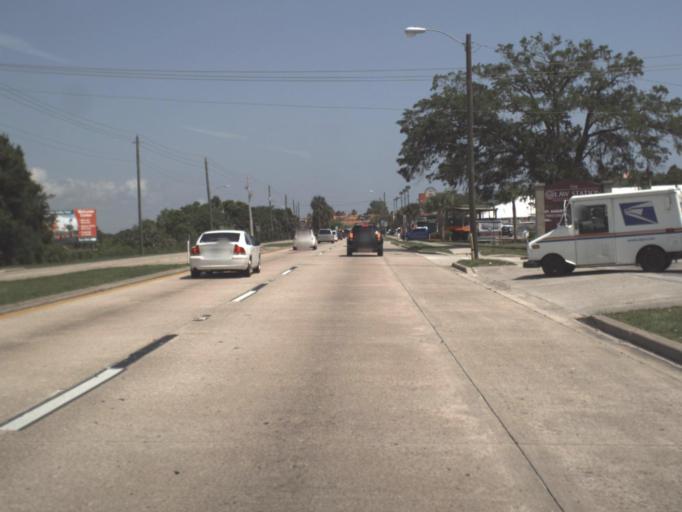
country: US
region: Florida
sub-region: Saint Johns County
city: Saint Augustine
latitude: 29.9064
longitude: -81.3213
